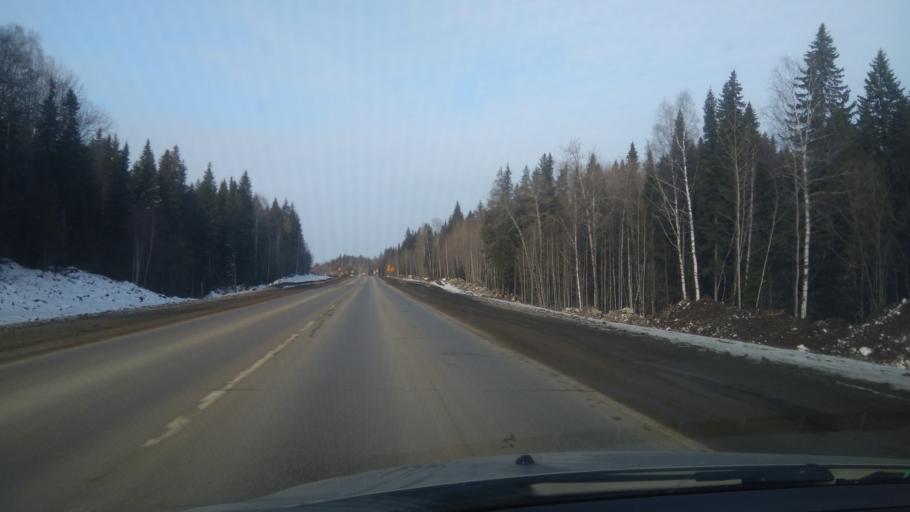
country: RU
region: Sverdlovsk
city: Bisert'
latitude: 56.8288
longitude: 59.1384
